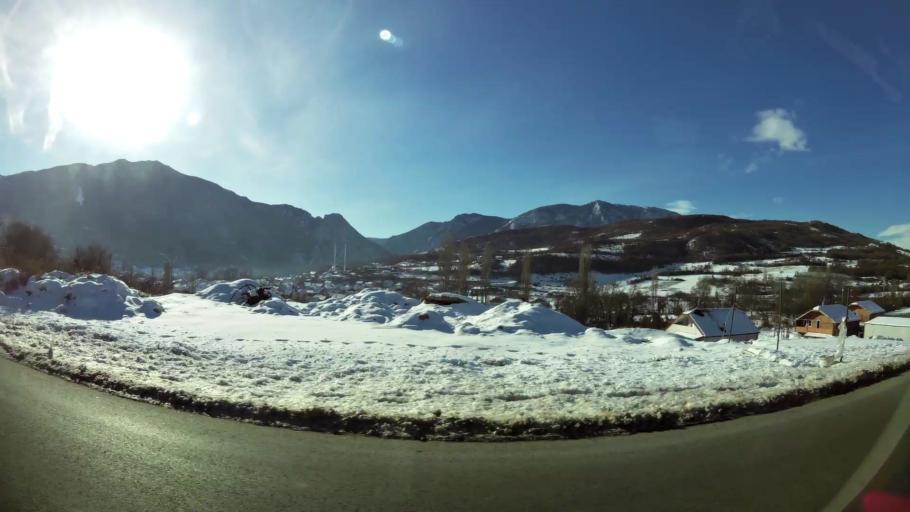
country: MK
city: Ljubin
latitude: 41.9855
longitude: 21.3035
